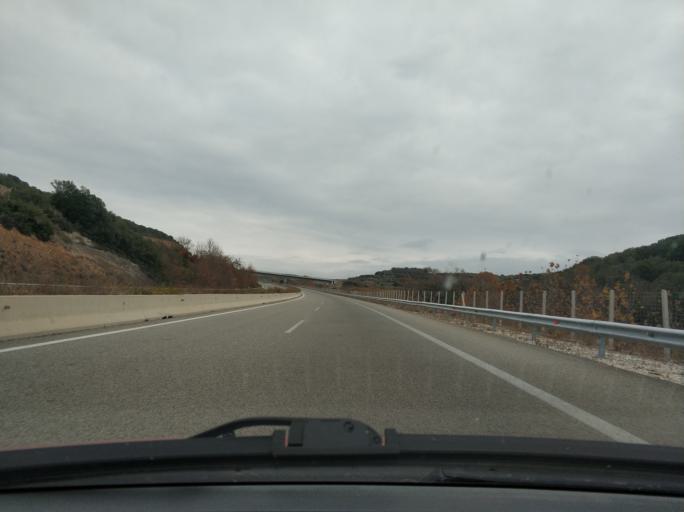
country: GR
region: East Macedonia and Thrace
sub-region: Nomos Kavalas
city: Paralia Ofryniou
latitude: 40.7918
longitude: 23.9982
